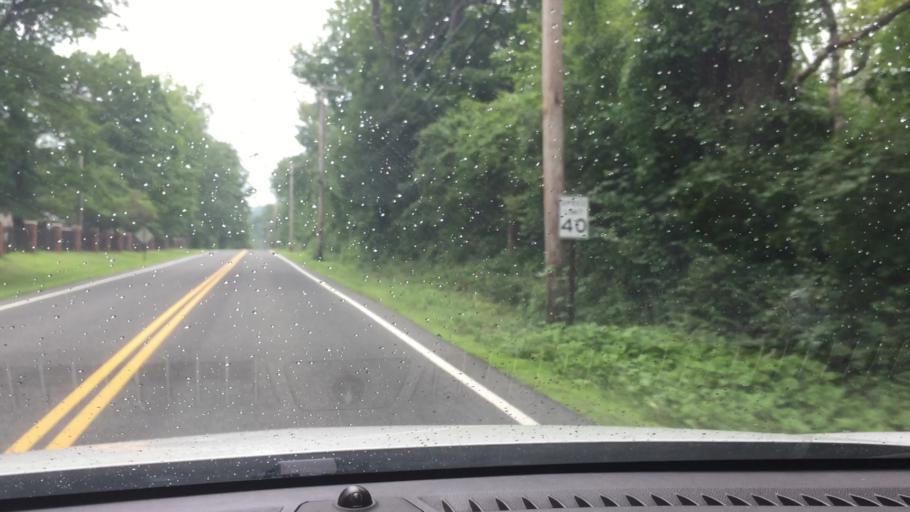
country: US
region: Massachusetts
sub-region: Berkshire County
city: Lenox
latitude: 42.3719
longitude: -73.2594
